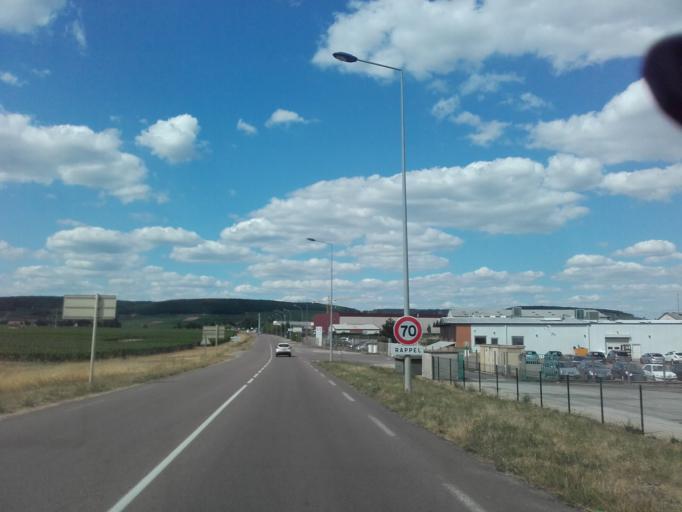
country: FR
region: Bourgogne
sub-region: Departement de la Cote-d'Or
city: Beaune
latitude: 47.0464
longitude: 4.8395
